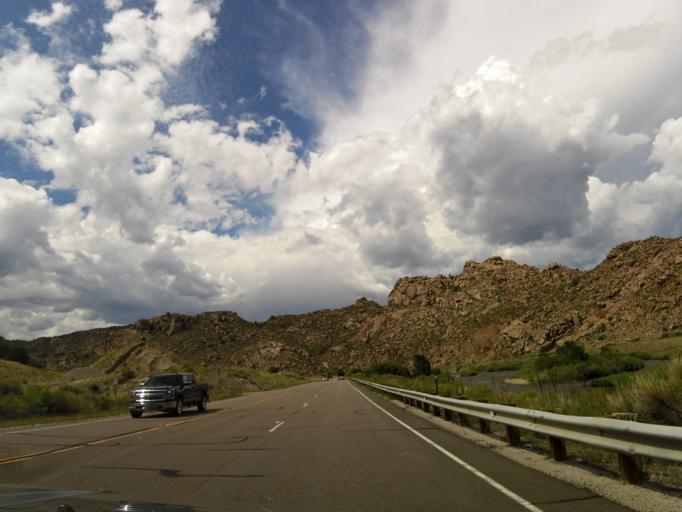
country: US
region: Colorado
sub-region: Custer County
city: Westcliffe
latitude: 38.3937
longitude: -105.6275
